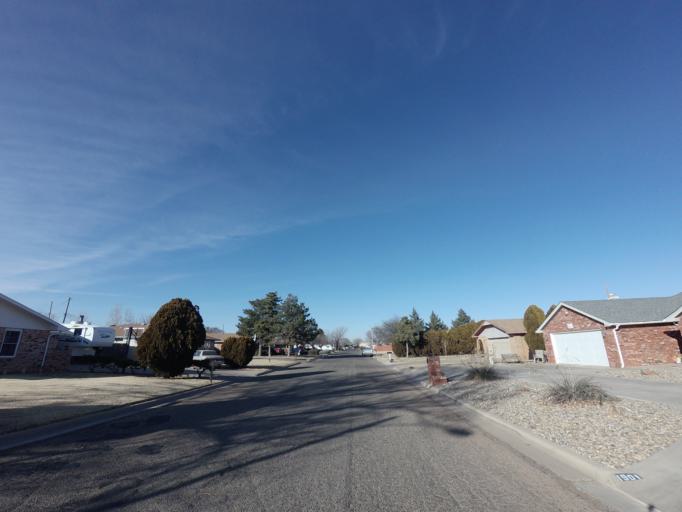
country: US
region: New Mexico
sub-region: Curry County
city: Clovis
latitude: 34.4160
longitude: -103.2285
